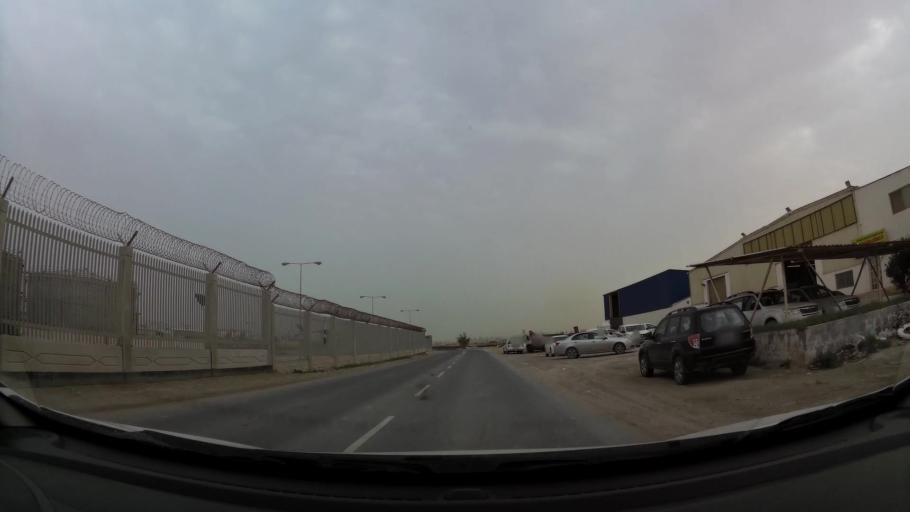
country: BH
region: Northern
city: Ar Rifa'
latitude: 26.1186
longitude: 50.5872
